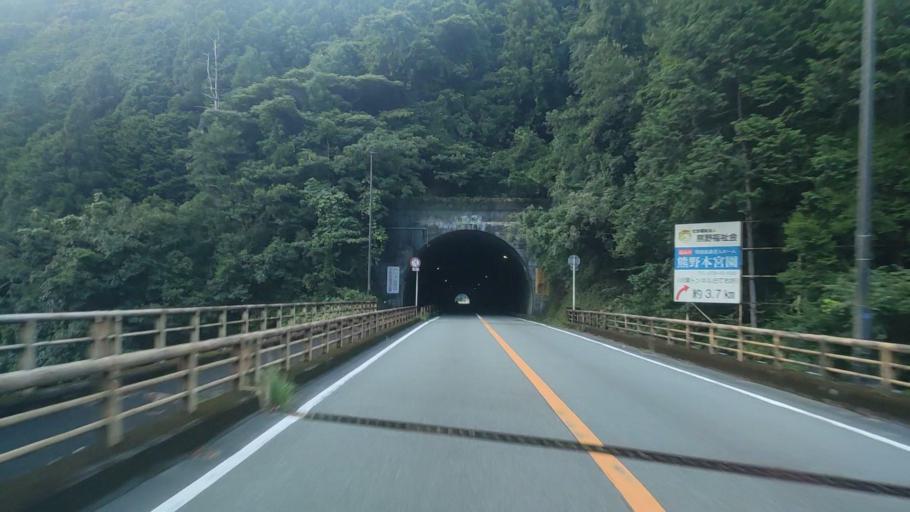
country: JP
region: Wakayama
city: Shingu
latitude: 33.8161
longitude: 135.7566
